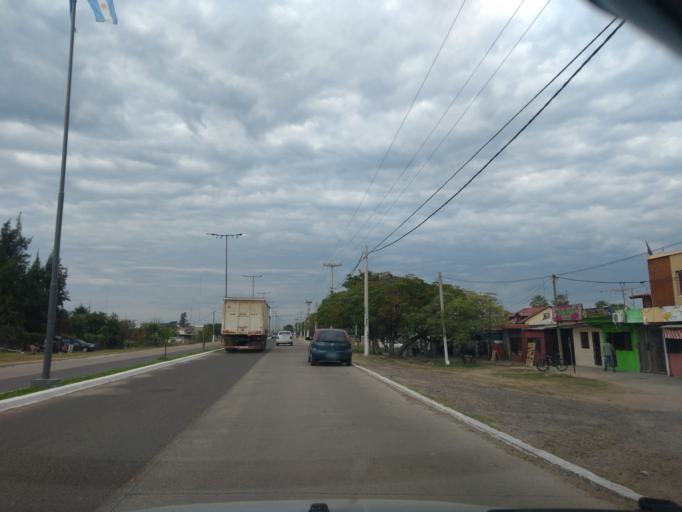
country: AR
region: Chaco
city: Puerto Vilelas
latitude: -27.5139
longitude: -58.9420
